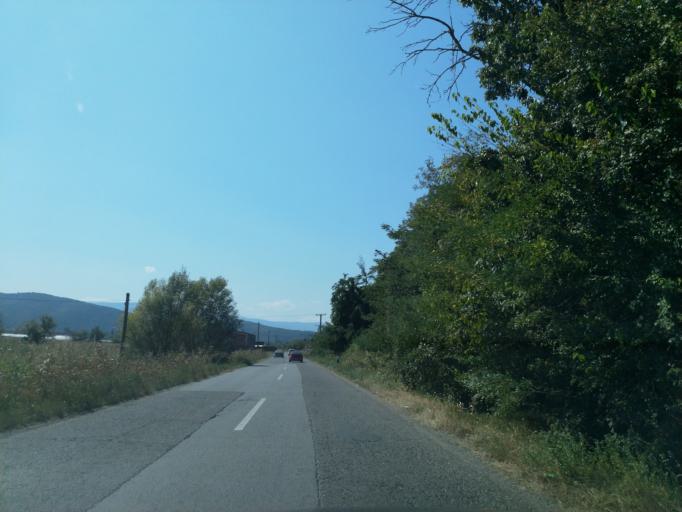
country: RS
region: Central Serbia
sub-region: Rasinski Okrug
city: Trstenik
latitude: 43.6317
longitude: 21.0095
